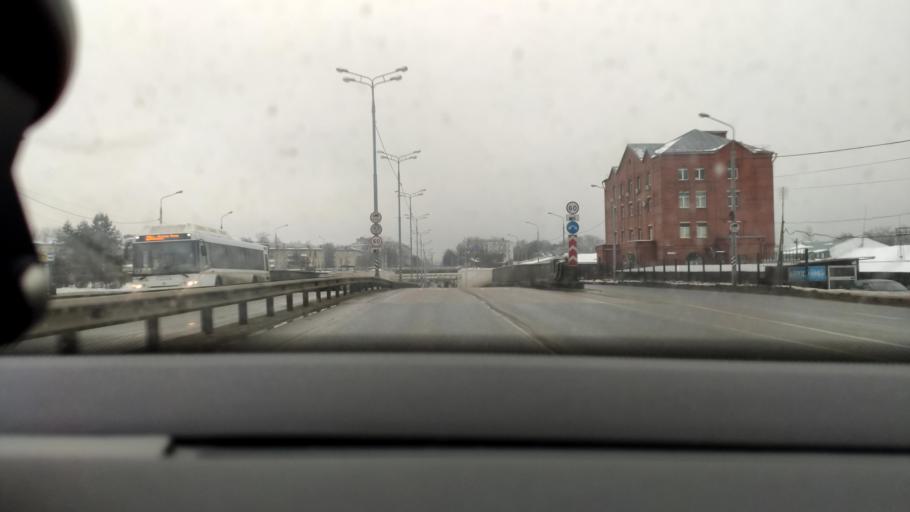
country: RU
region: Moskovskaya
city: Sergiyev Posad
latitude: 56.2890
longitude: 38.1263
